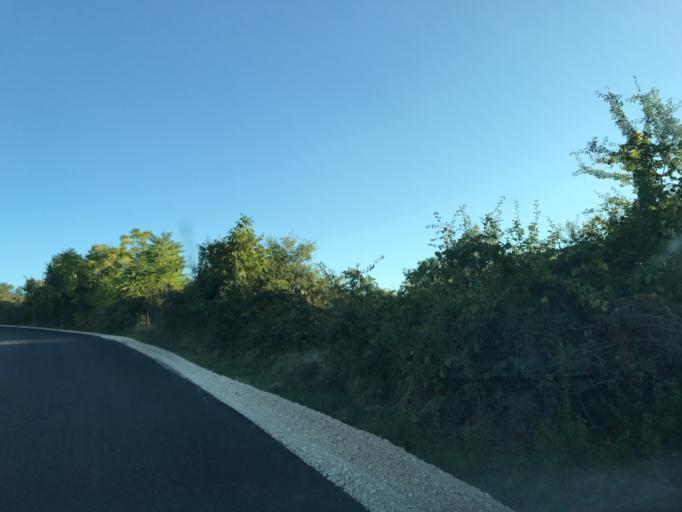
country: BG
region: Vidin
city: Bregovo
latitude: 44.1307
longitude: 22.5983
